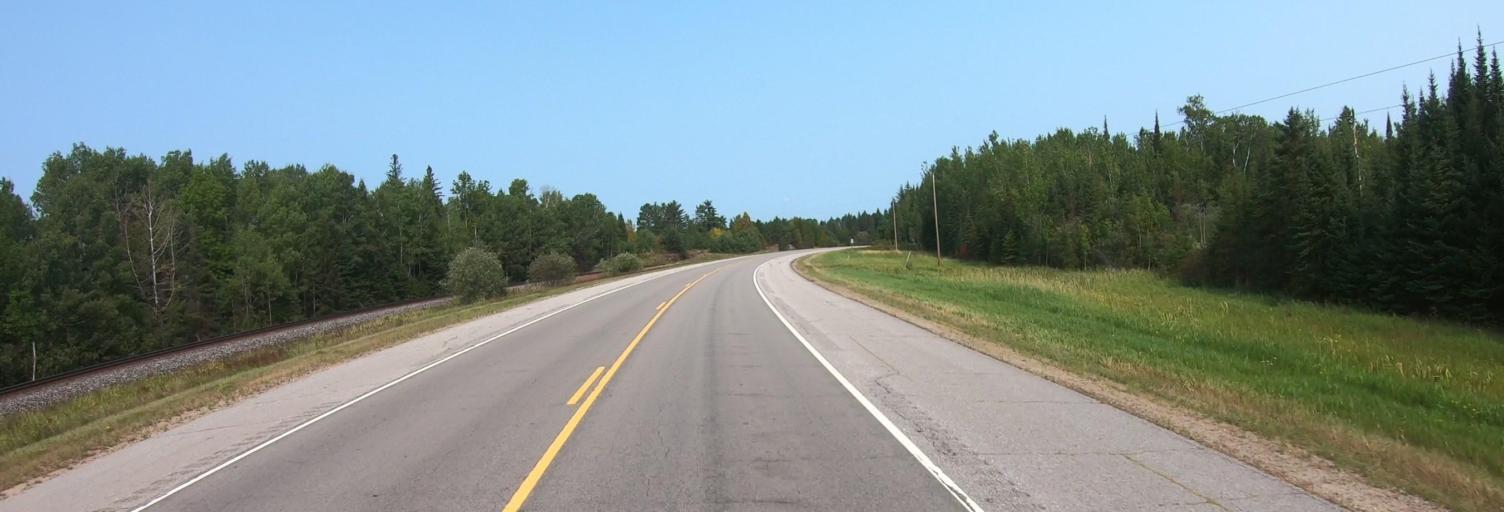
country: US
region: Minnesota
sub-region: Saint Louis County
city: Mountain Iron
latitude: 48.0966
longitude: -92.8432
